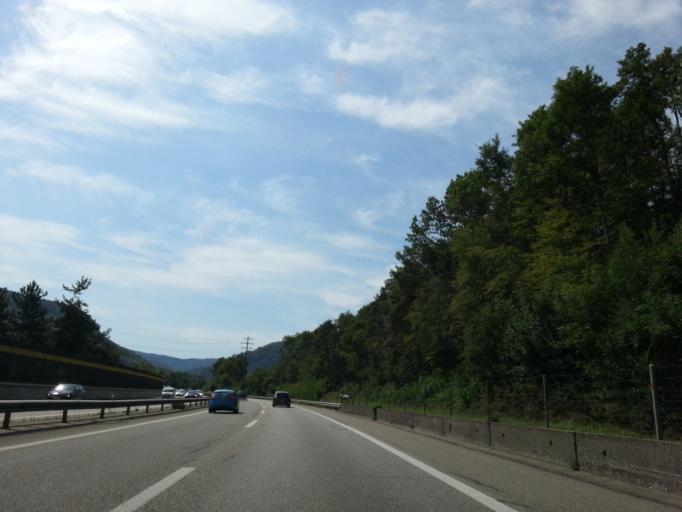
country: CH
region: Basel-Landschaft
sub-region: Bezirk Waldenburg
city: Diegten
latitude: 47.4180
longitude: 7.8080
